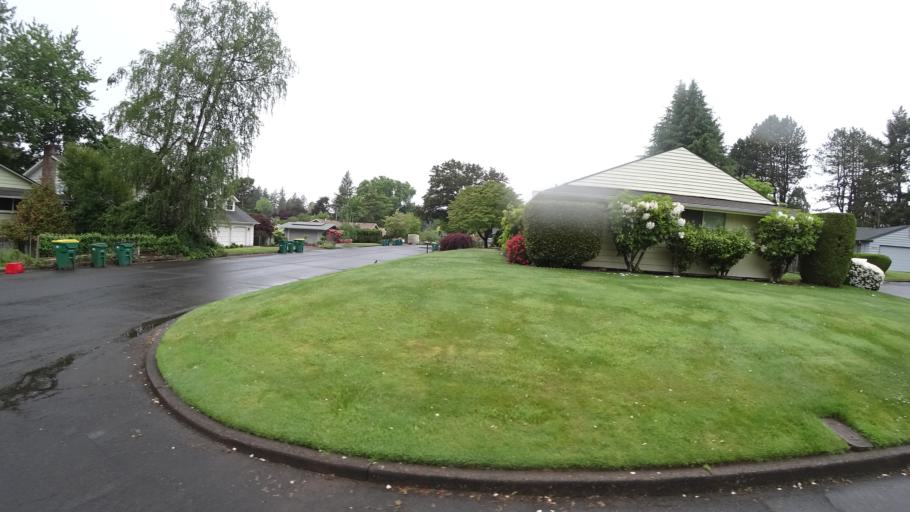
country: US
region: Oregon
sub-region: Washington County
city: Raleigh Hills
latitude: 45.4824
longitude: -122.7687
